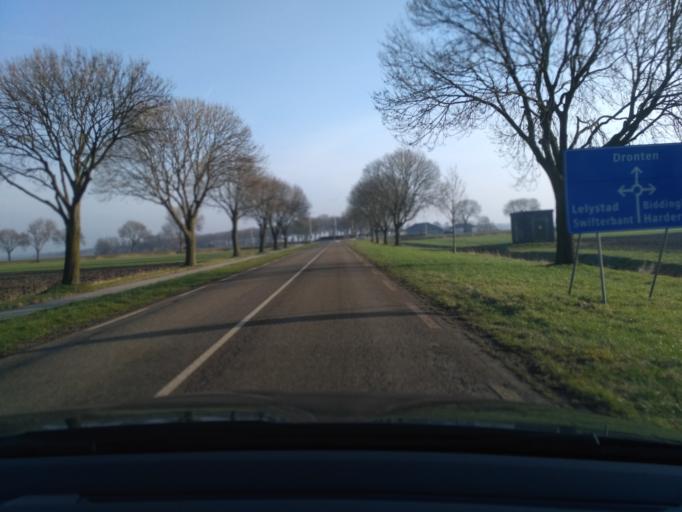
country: NL
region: Flevoland
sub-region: Gemeente Dronten
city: Biddinghuizen
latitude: 52.4814
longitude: 5.6622
